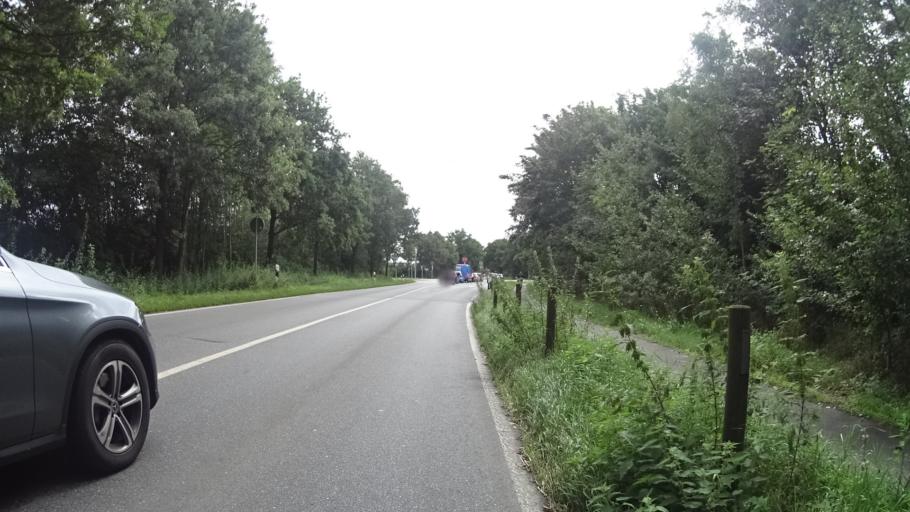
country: DE
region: Schleswig-Holstein
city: Tangstedt
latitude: 53.7286
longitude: 10.0986
